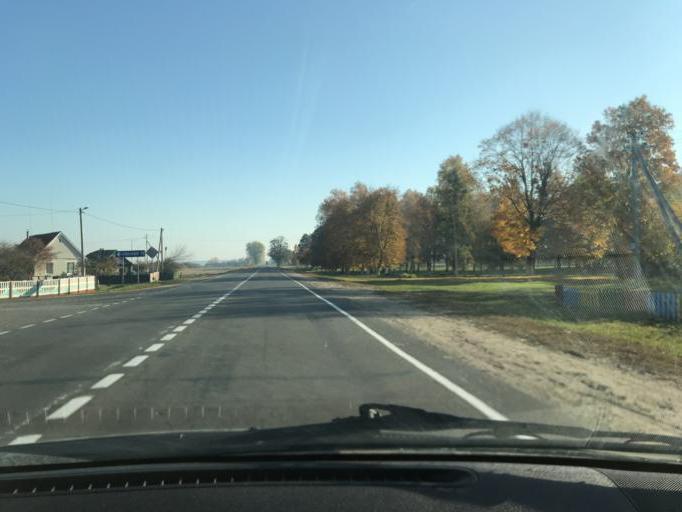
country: BY
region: Brest
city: Baranovichi
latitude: 52.8962
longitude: 25.8510
